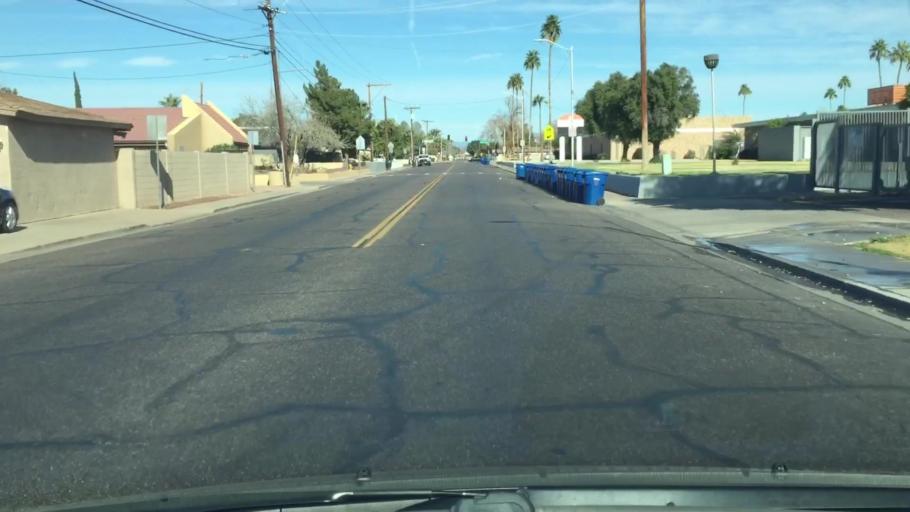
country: US
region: Arizona
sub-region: Maricopa County
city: Mesa
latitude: 33.4273
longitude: -111.8523
